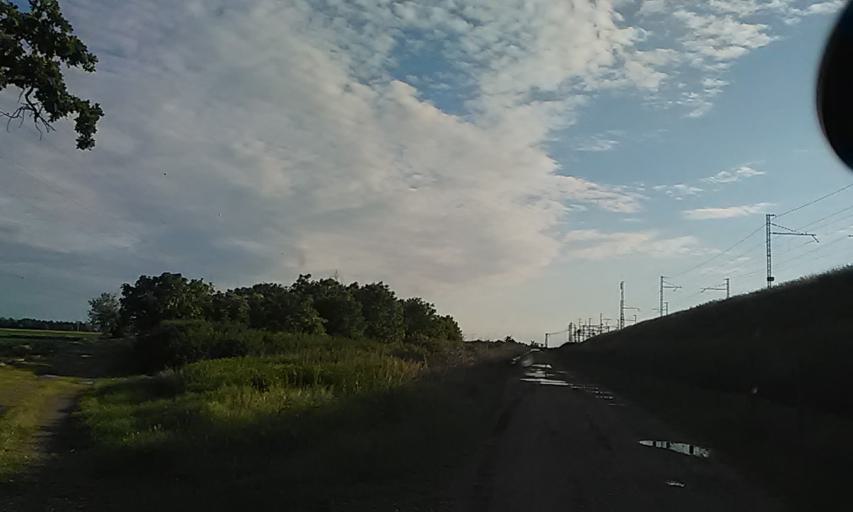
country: IT
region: Piedmont
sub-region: Provincia di Vercelli
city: Santhia
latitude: 45.3696
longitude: 8.1298
